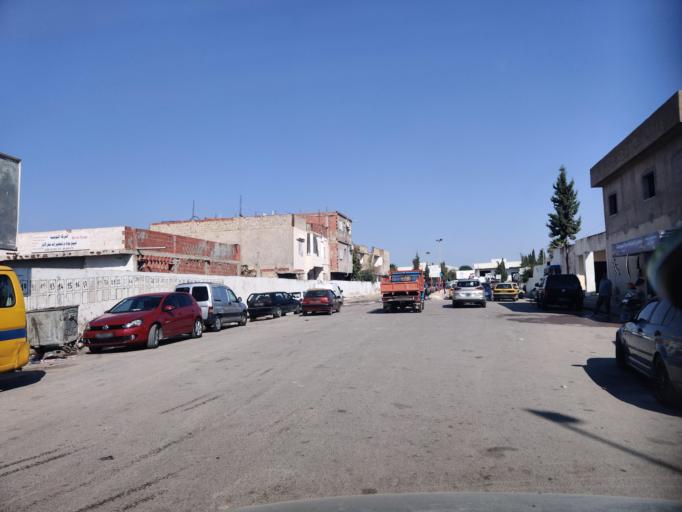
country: TN
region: Manouba
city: Manouba
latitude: 36.7796
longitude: 10.1170
